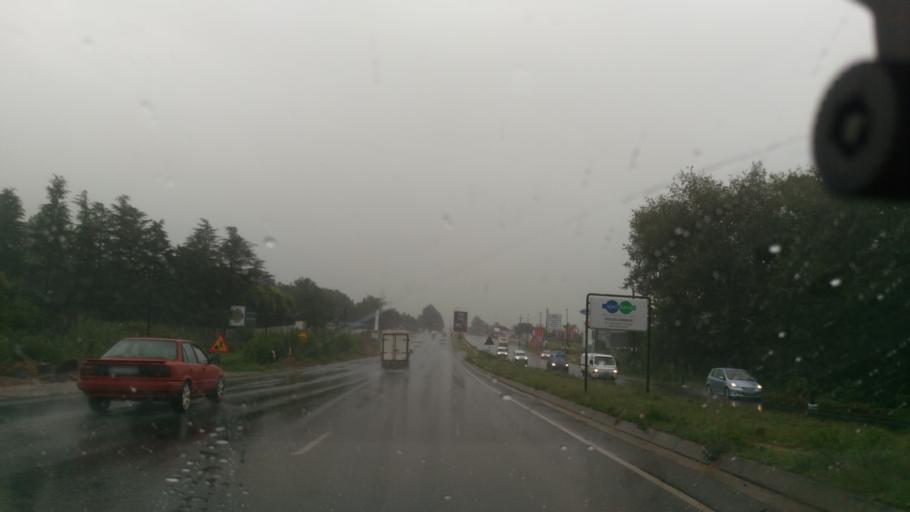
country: ZA
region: Gauteng
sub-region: City of Johannesburg Metropolitan Municipality
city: Diepsloot
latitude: -26.0242
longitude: 27.9949
